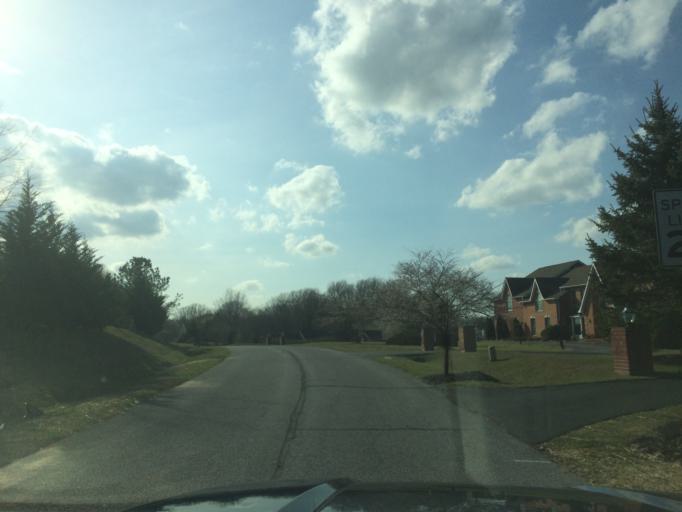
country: US
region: Maryland
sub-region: Howard County
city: Highland
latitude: 39.2075
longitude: -76.9476
